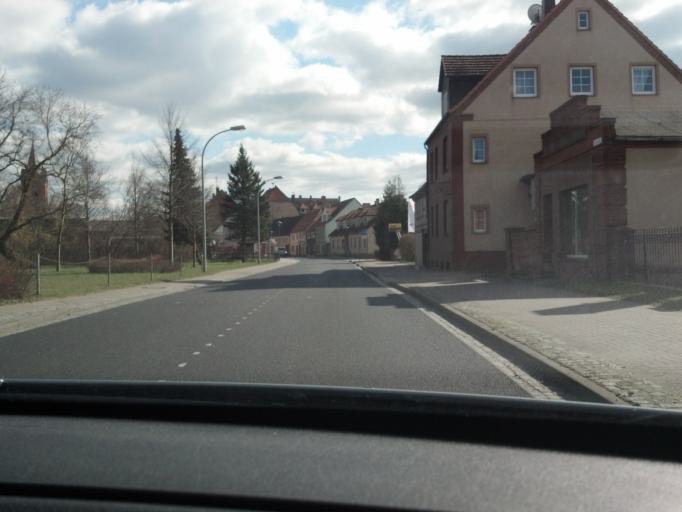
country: DE
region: Brandenburg
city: Gerdshagen
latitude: 53.3171
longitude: 12.2409
